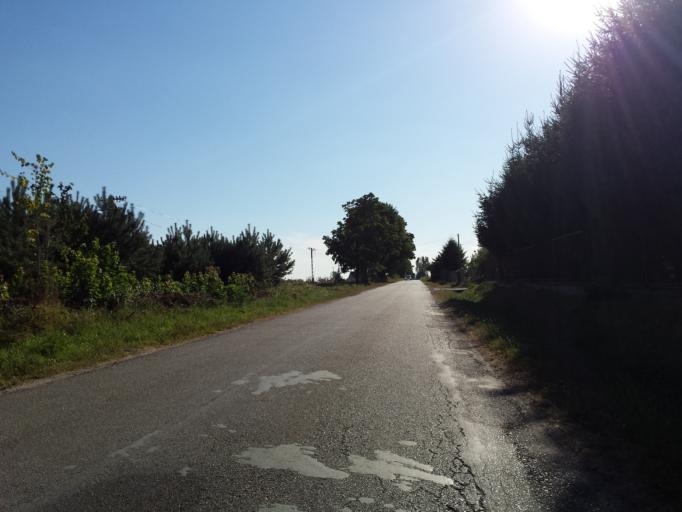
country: PL
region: Swietokrzyskie
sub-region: Powiat buski
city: Gnojno
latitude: 50.6564
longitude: 20.8350
